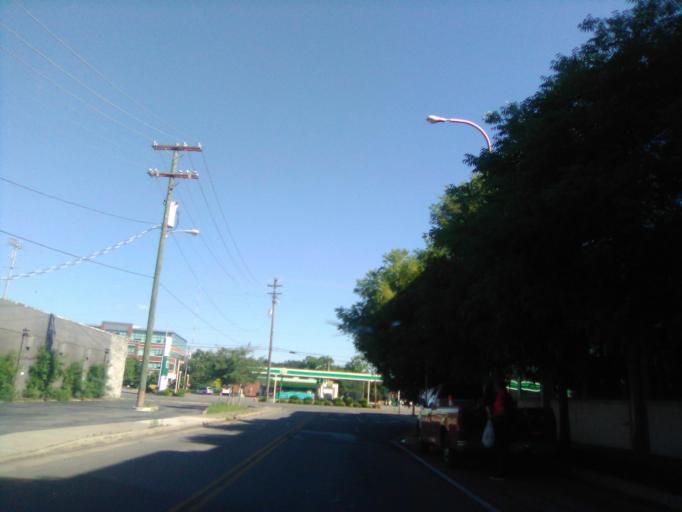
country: US
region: Tennessee
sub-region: Davidson County
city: Belle Meade
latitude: 36.1259
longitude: -86.8450
